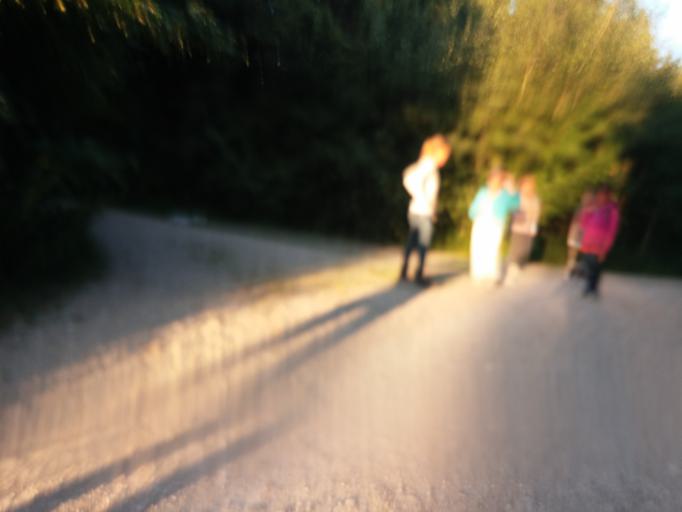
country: DE
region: Bavaria
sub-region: Upper Bavaria
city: Putzbrunn
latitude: 48.0947
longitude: 11.7011
